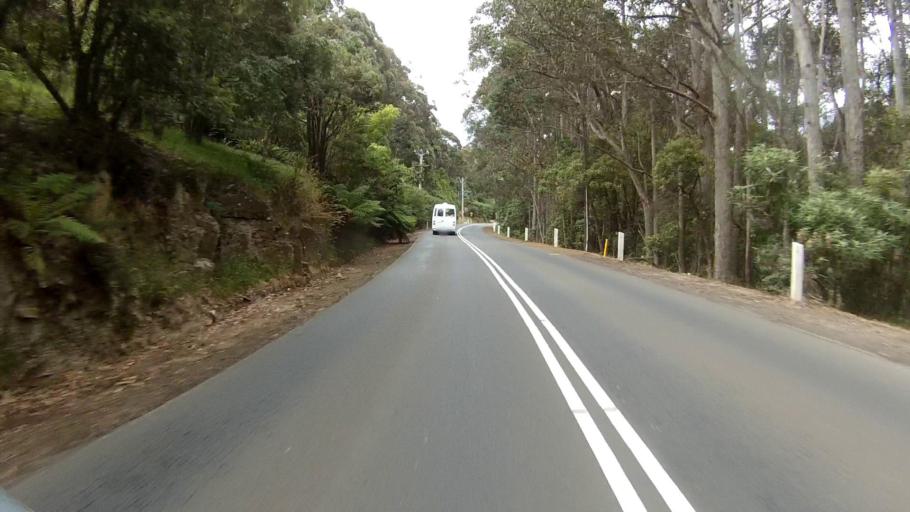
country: AU
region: Tasmania
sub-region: Hobart
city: Dynnyrne
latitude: -42.9201
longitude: 147.2676
